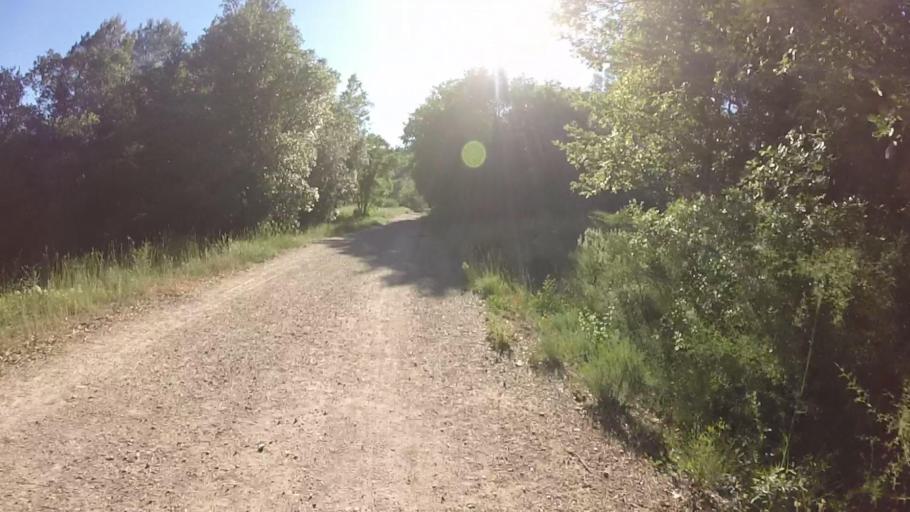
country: FR
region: Provence-Alpes-Cote d'Azur
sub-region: Departement des Alpes-Maritimes
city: Mougins
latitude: 43.6106
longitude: 7.0317
